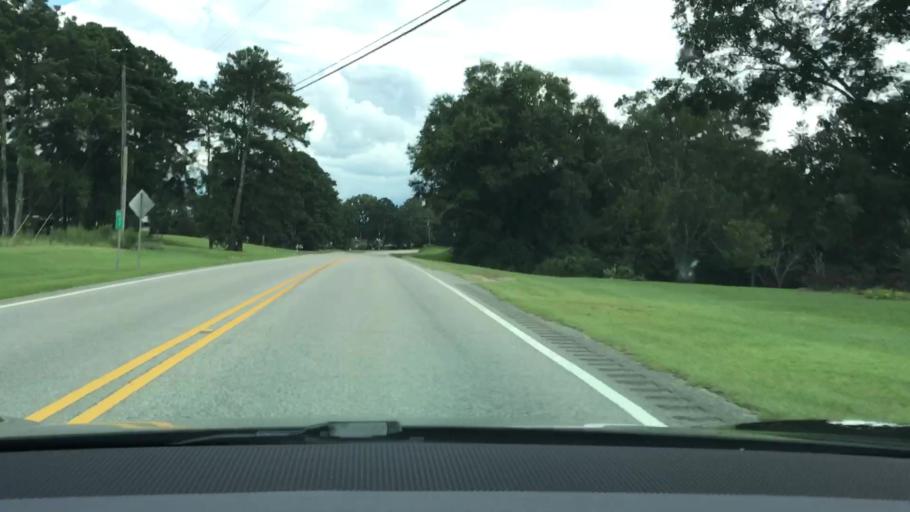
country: US
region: Alabama
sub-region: Coffee County
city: Elba
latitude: 31.5917
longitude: -86.0036
